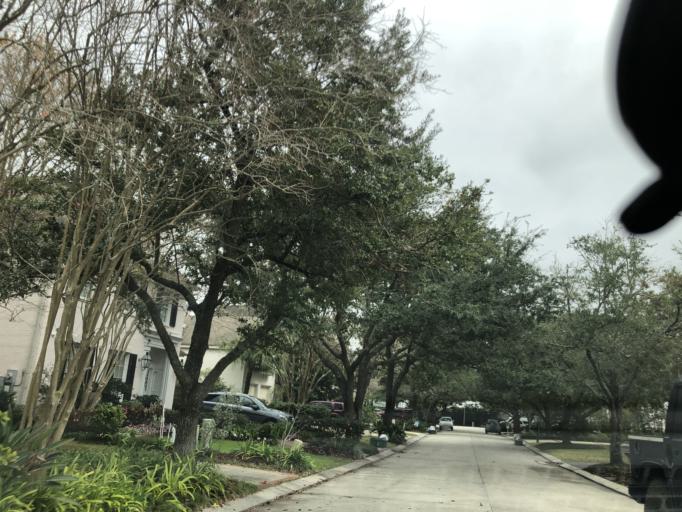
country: US
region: Louisiana
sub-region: Jefferson Parish
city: Metairie
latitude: 29.9785
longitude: -90.1519
